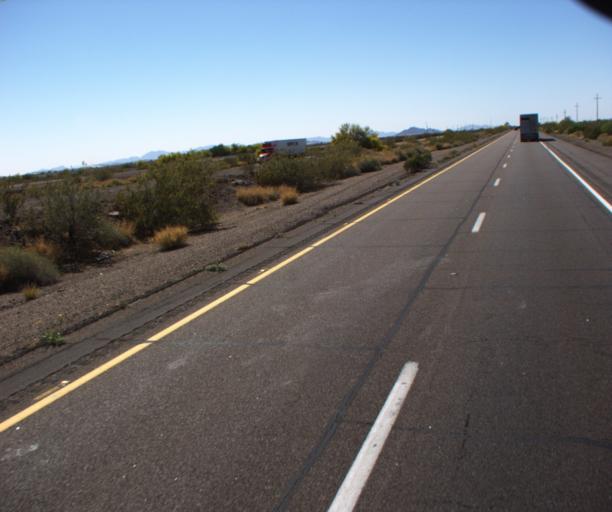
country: US
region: Arizona
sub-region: Maricopa County
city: Gila Bend
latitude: 32.8400
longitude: -113.3245
